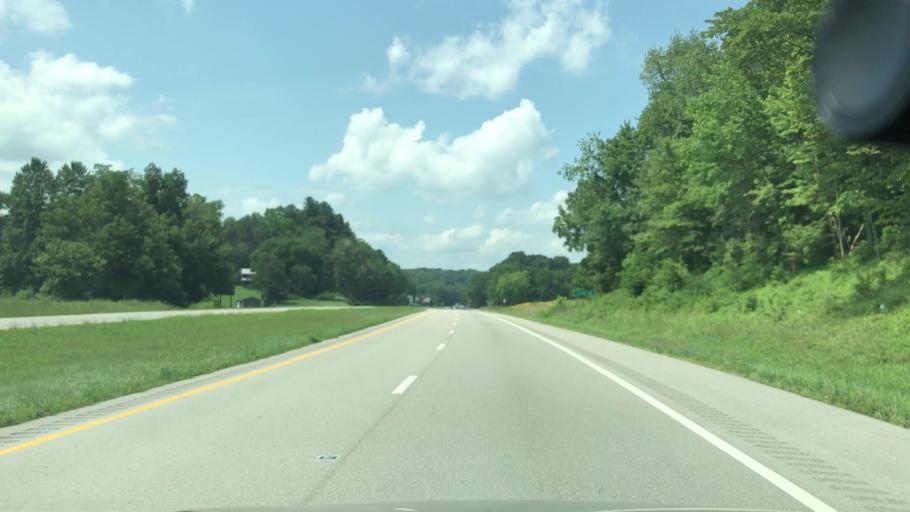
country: US
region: Ohio
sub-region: Jackson County
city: Oak Hill
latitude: 38.8998
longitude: -82.4429
